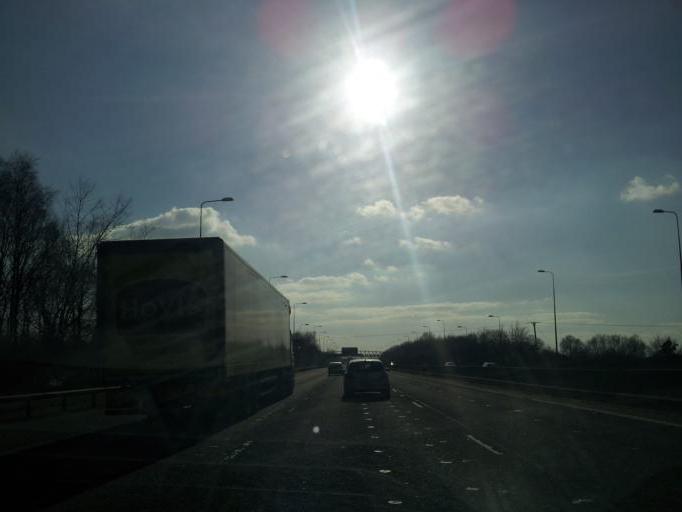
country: GB
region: England
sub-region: South Gloucestershire
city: Severn Beach
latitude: 51.5114
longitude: -2.6550
